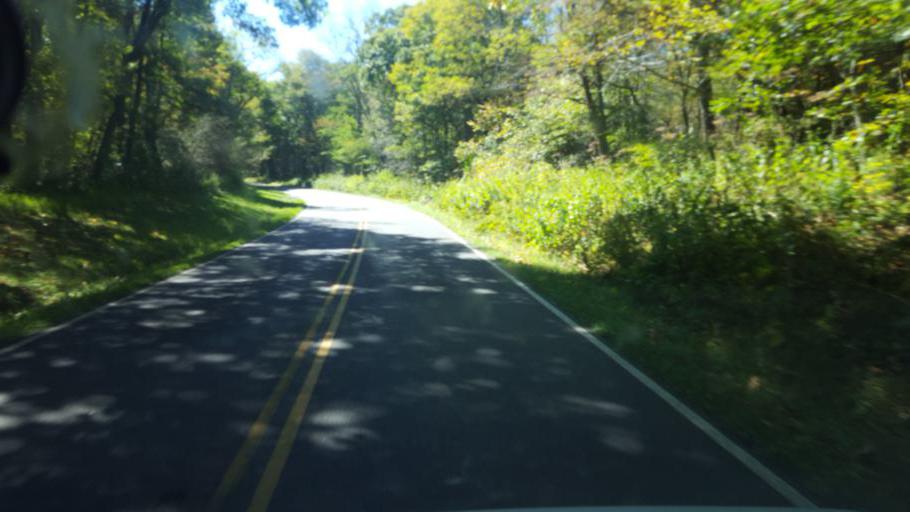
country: US
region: Virginia
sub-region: Greene County
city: Stanardsville
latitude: 38.4145
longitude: -78.4889
